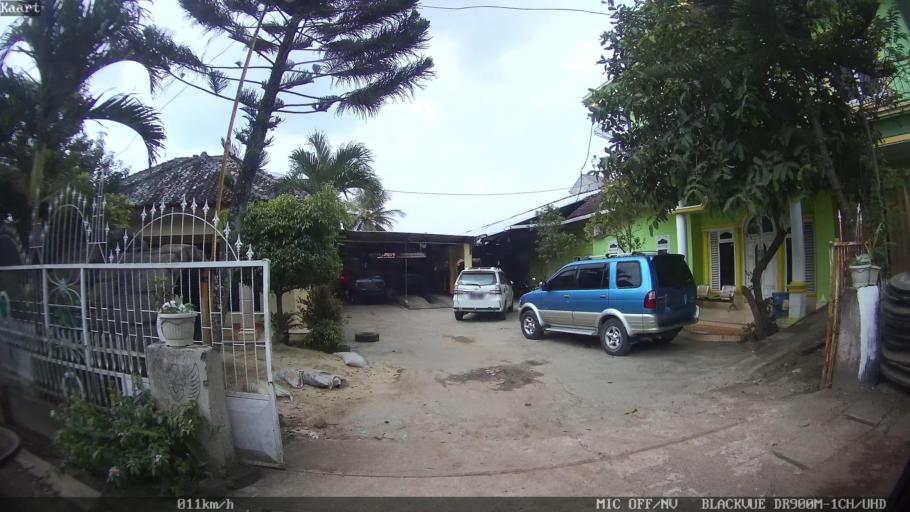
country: ID
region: Lampung
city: Gadingrejo
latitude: -5.3710
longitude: 105.0609
